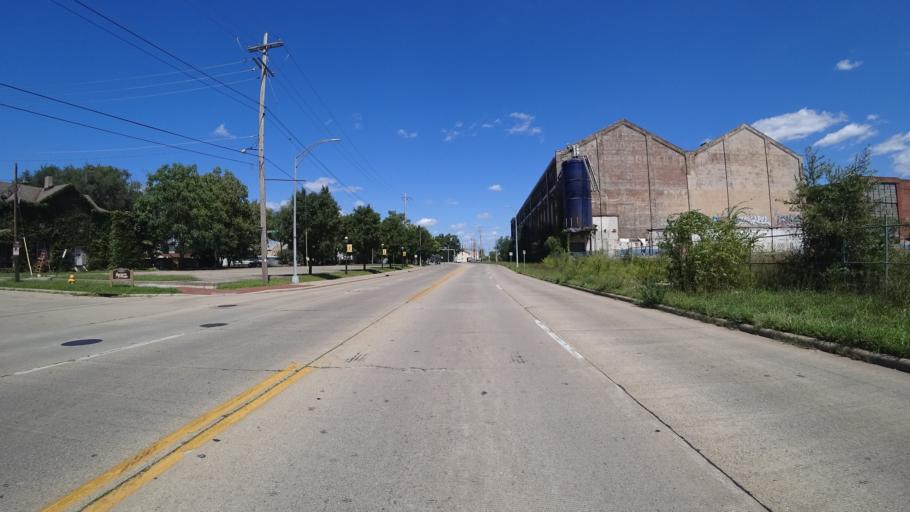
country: US
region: Ohio
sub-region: Butler County
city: Hamilton
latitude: 39.4021
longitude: -84.5572
